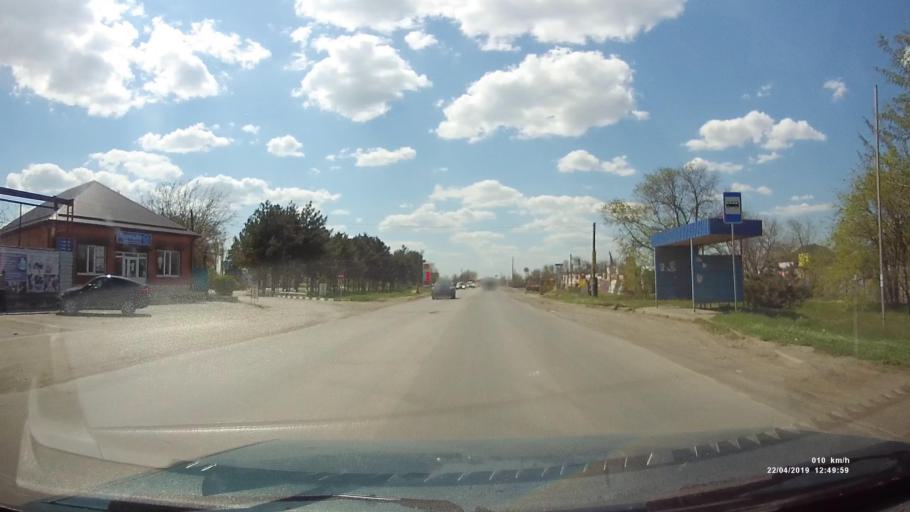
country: RU
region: Rostov
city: Azov
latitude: 47.0906
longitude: 39.3927
